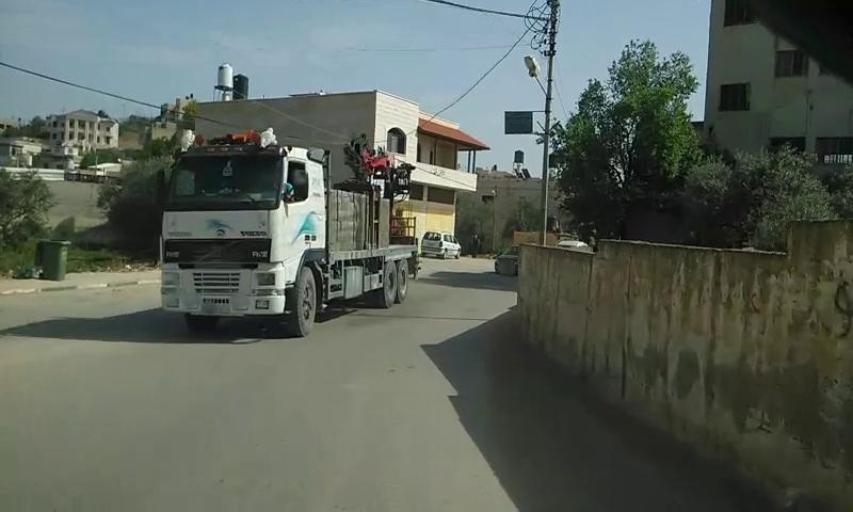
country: PS
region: West Bank
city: Birqin
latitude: 32.4507
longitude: 35.2628
